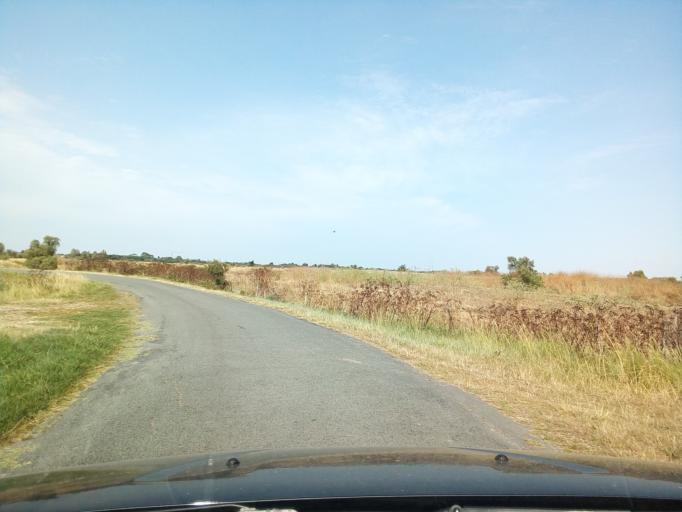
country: FR
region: Poitou-Charentes
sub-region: Departement de la Charente-Maritime
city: Dolus-d'Oleron
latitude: 45.9518
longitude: -1.2838
